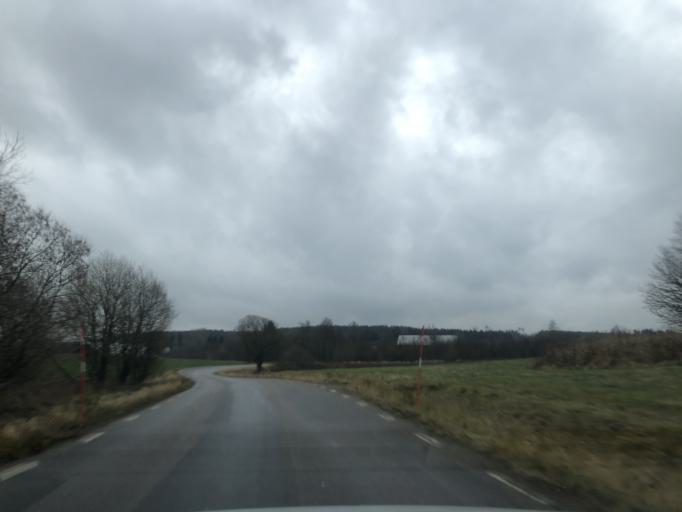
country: SE
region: Vaestra Goetaland
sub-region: Ulricehamns Kommun
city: Ulricehamn
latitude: 57.8864
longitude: 13.5120
